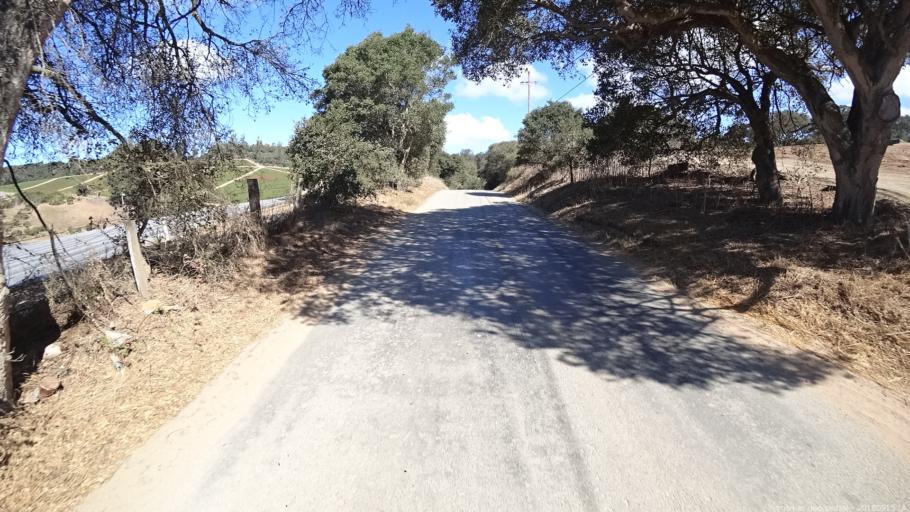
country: US
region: California
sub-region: Monterey County
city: Las Lomas
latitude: 36.8703
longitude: -121.7226
